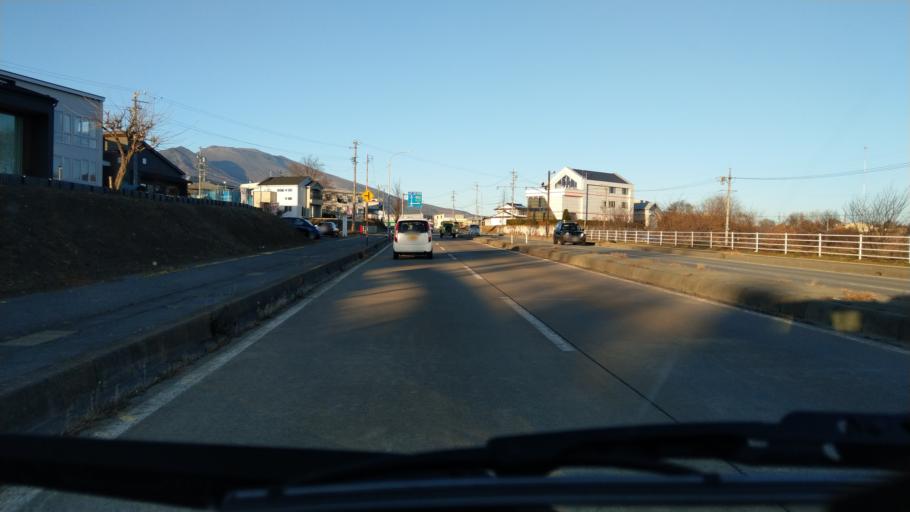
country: JP
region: Nagano
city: Komoro
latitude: 36.2834
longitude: 138.4728
